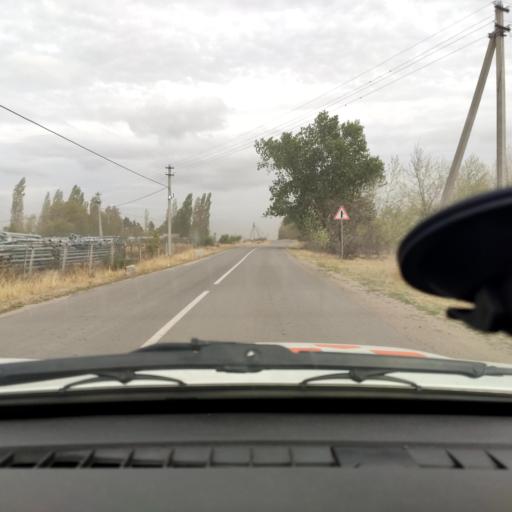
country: RU
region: Lipetsk
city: Khlevnoye
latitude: 52.0054
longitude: 39.1219
